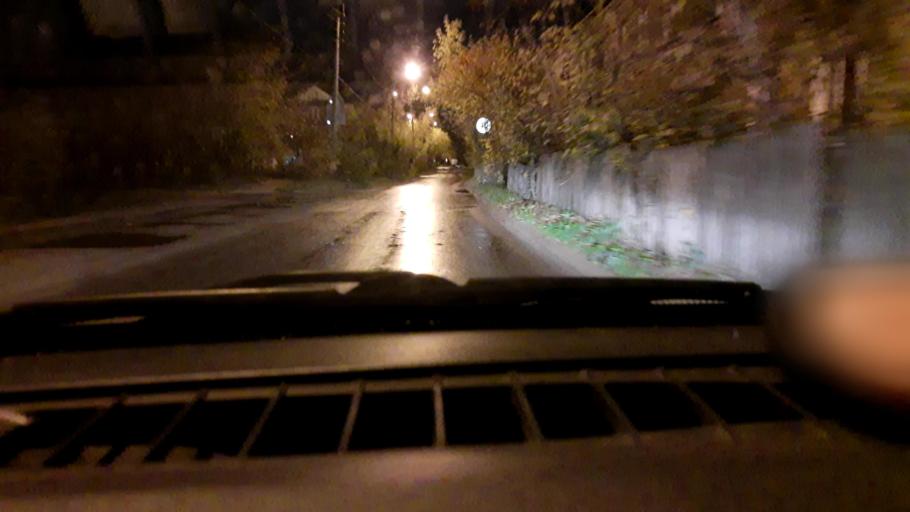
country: RU
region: Nizjnij Novgorod
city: Gorbatovka
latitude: 56.2410
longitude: 43.8369
